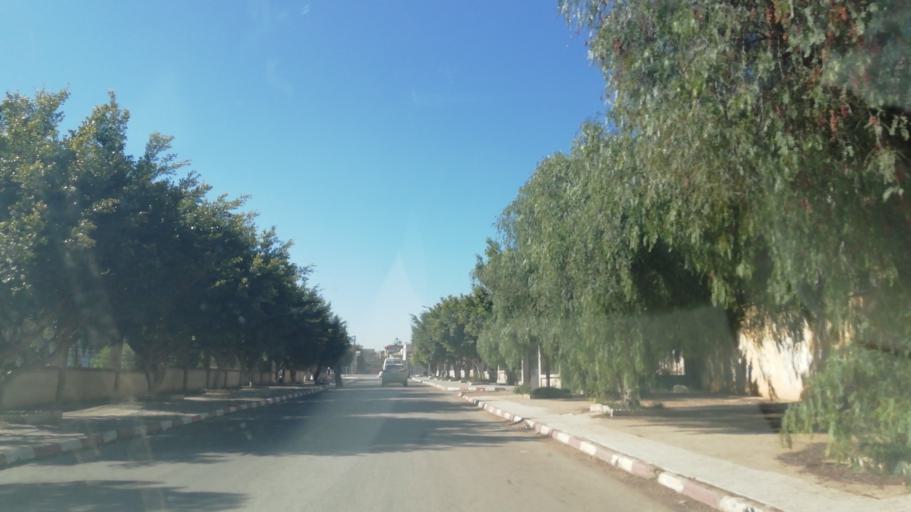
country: DZ
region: Oran
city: Es Senia
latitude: 35.6628
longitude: -0.6311
